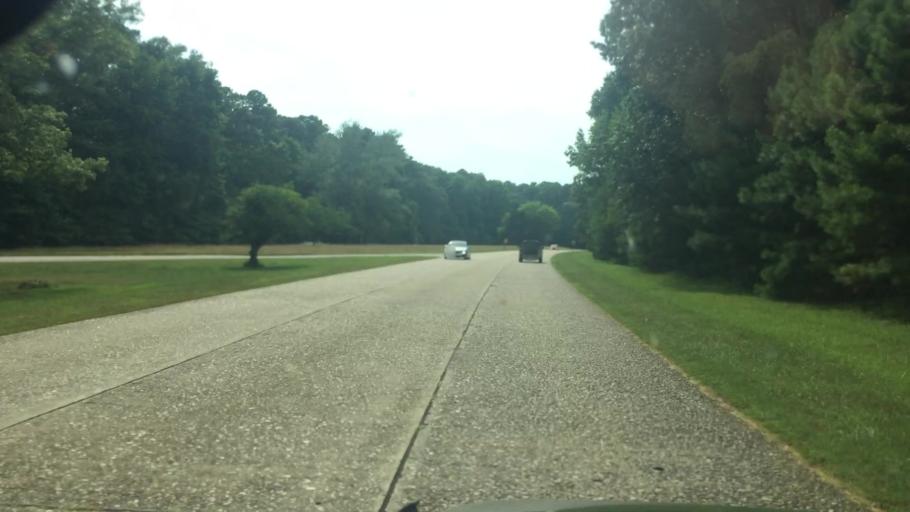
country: US
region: Virginia
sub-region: James City County
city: Williamsburg
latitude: 37.2170
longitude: -76.7570
